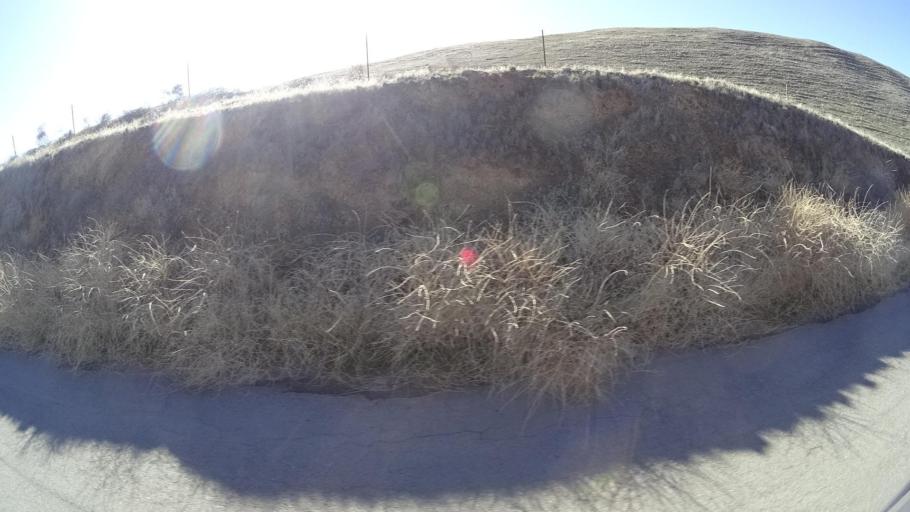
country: US
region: California
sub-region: Kern County
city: Maricopa
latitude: 34.9739
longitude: -119.4597
